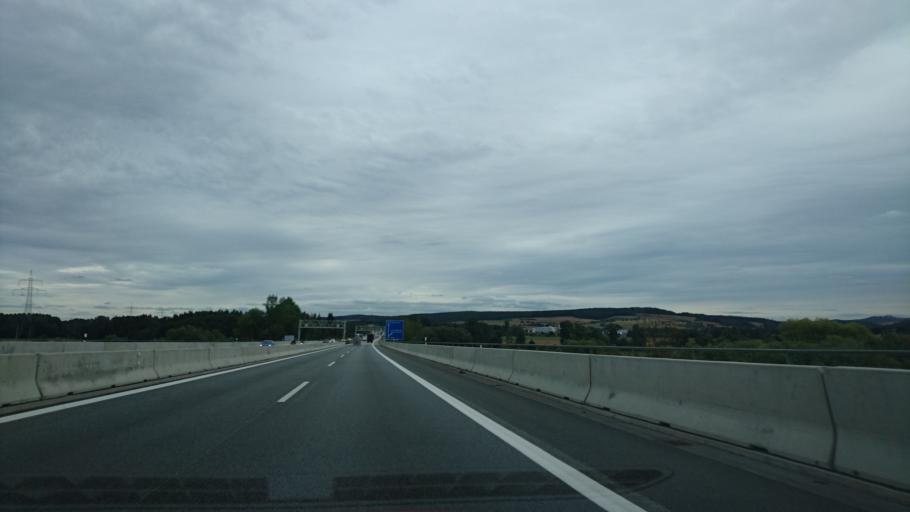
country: DE
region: Bavaria
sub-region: Upper Palatinate
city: Luhe-Wildenau
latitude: 49.5849
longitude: 12.1321
